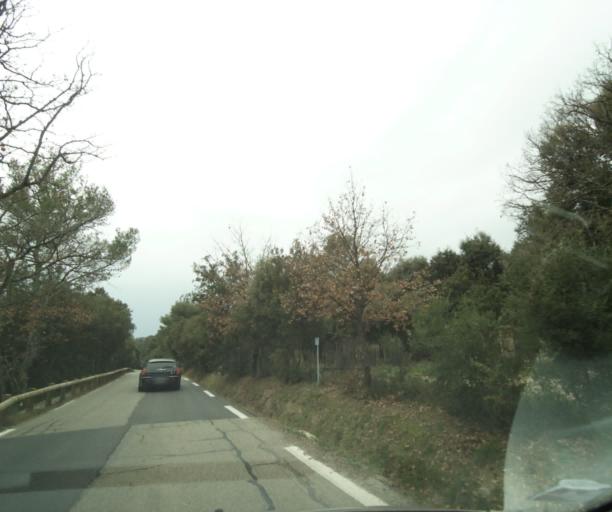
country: FR
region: Provence-Alpes-Cote d'Azur
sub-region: Departement des Bouches-du-Rhone
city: Chateauneuf-le-Rouge
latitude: 43.5546
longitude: 5.5861
